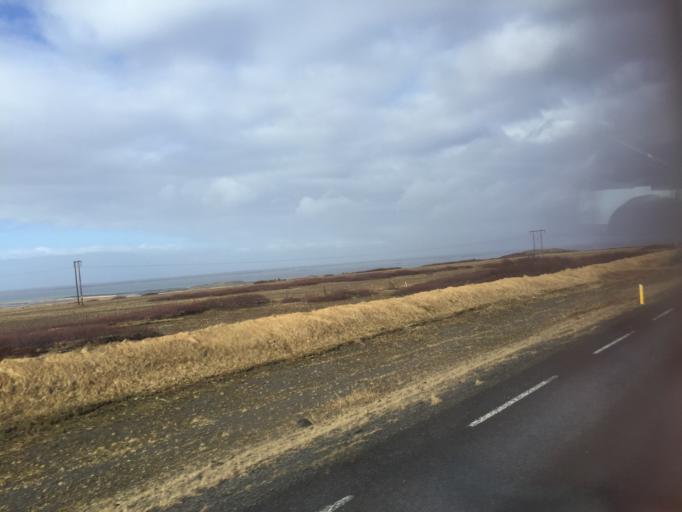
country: IS
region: West
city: Borgarnes
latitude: 64.4505
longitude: -21.9597
